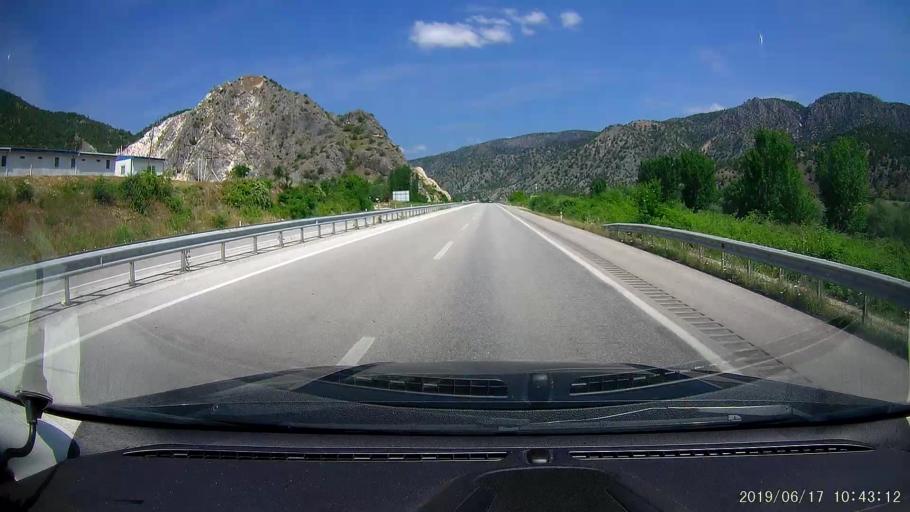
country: TR
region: Corum
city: Kargi
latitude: 41.0603
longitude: 34.5399
